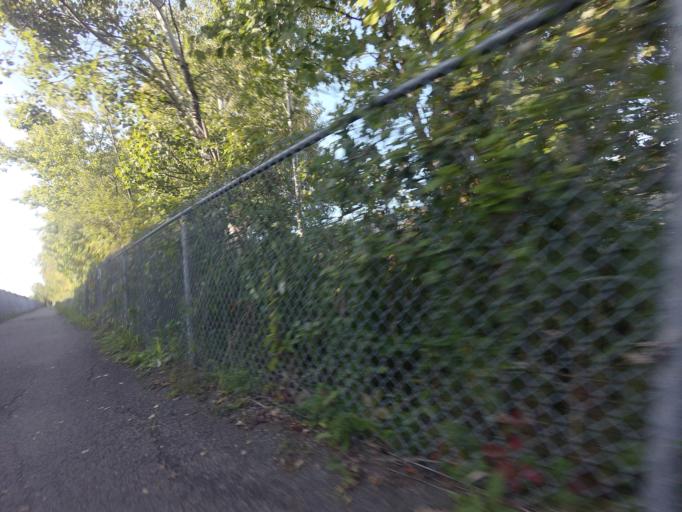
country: CA
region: Quebec
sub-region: Laurentides
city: Saint-Jerome
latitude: 45.7562
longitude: -73.9777
